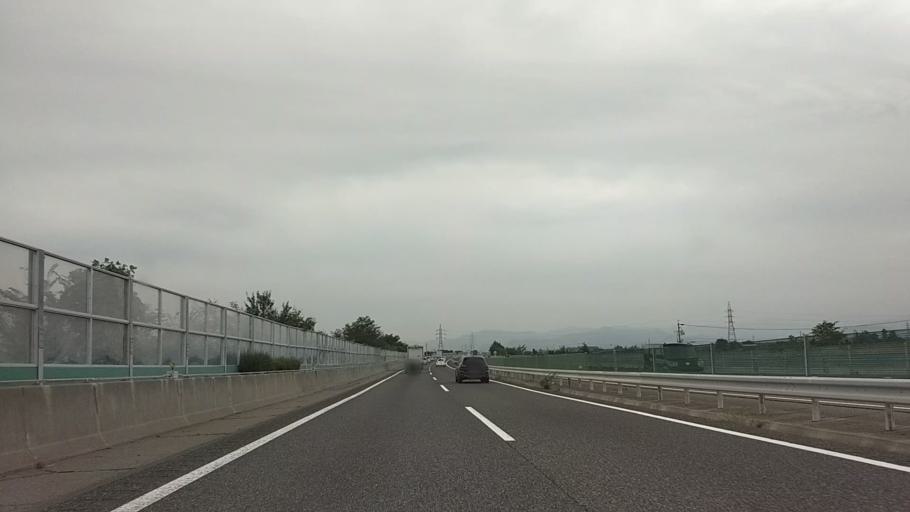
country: JP
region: Nagano
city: Matsumoto
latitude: 36.1989
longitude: 137.9347
